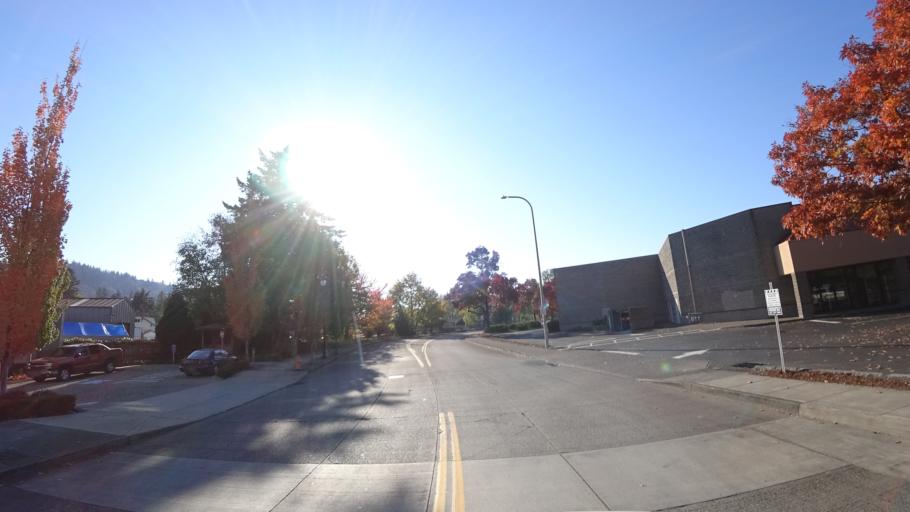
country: US
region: Oregon
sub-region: Multnomah County
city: Gresham
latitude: 45.4997
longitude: -122.4336
